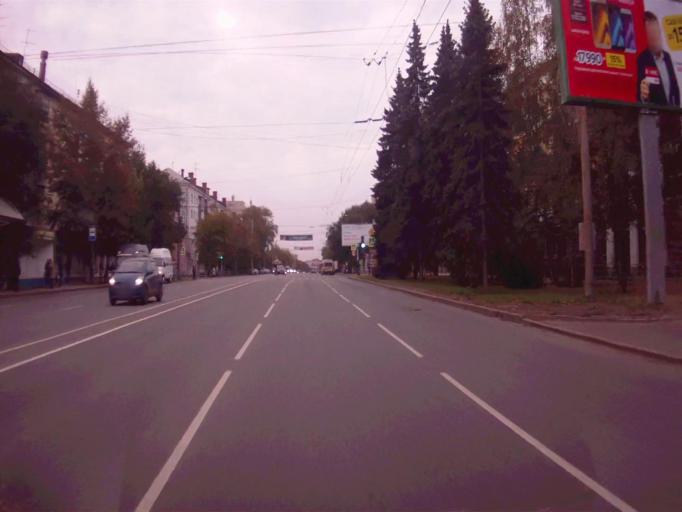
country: RU
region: Chelyabinsk
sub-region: Gorod Chelyabinsk
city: Chelyabinsk
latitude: 55.1565
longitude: 61.4133
